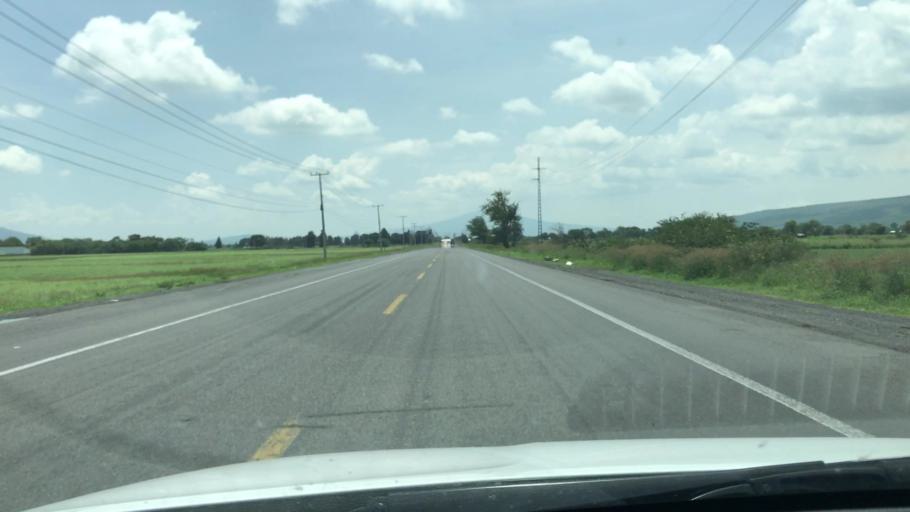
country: MX
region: Michoacan
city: Tanhuato de Guerrero
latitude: 20.2804
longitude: -102.3600
